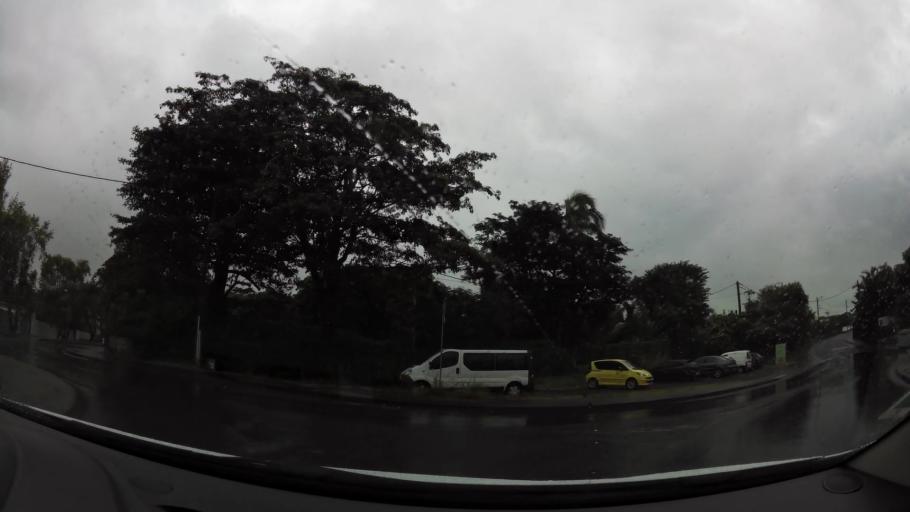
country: RE
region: Reunion
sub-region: Reunion
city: Saint-Andre
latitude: -20.9543
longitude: 55.6545
